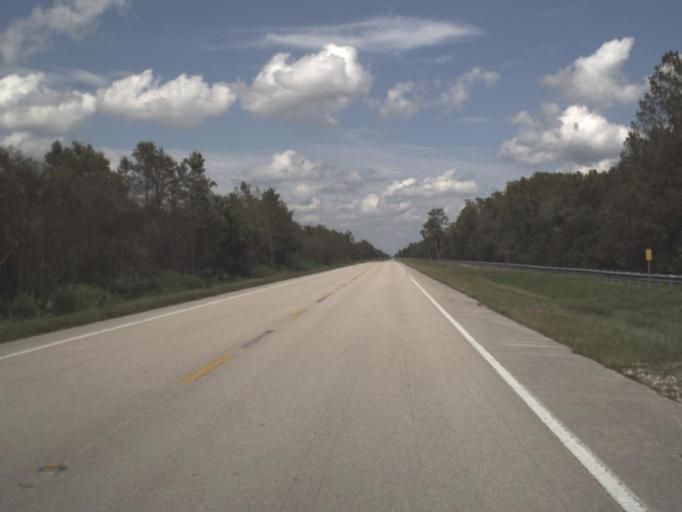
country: US
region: Florida
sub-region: Collier County
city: Orangetree
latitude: 26.0792
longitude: -81.3446
